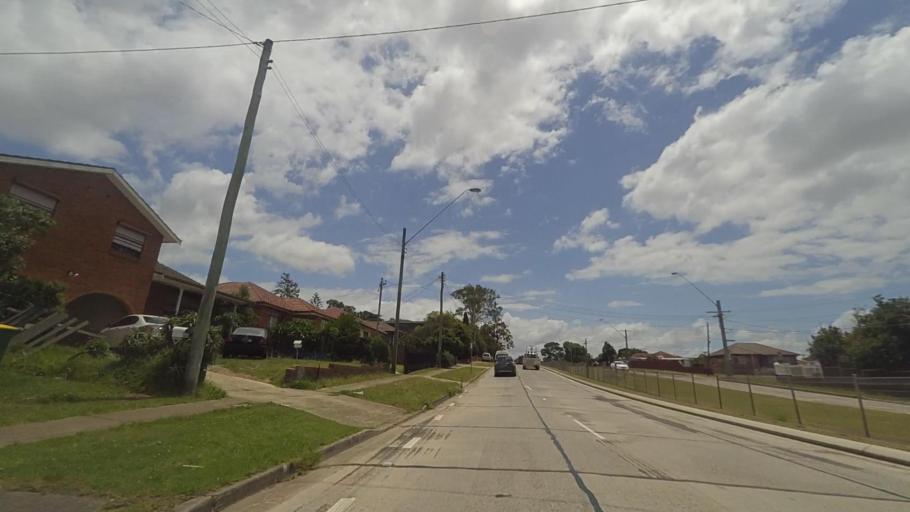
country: AU
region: New South Wales
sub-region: Fairfield
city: Cabramatta West
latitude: -33.8871
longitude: 150.9231
